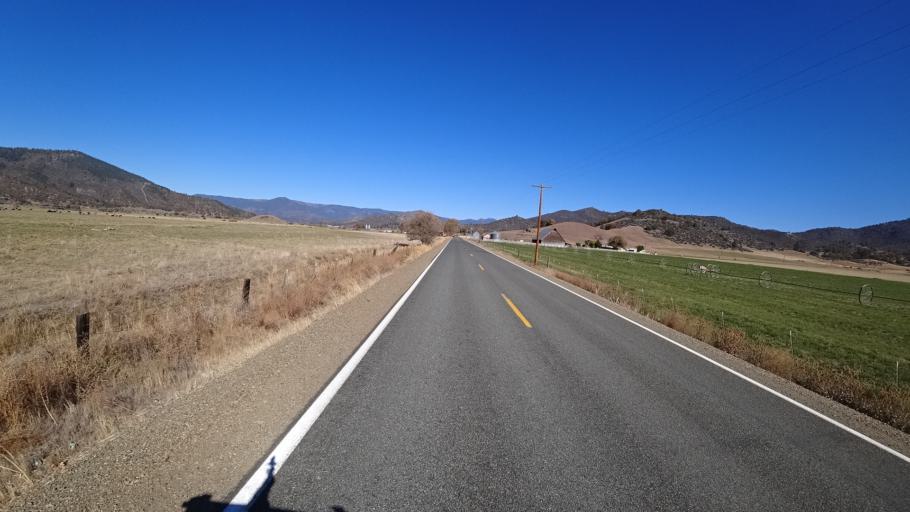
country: US
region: California
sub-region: Siskiyou County
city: Yreka
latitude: 41.5759
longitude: -122.8366
